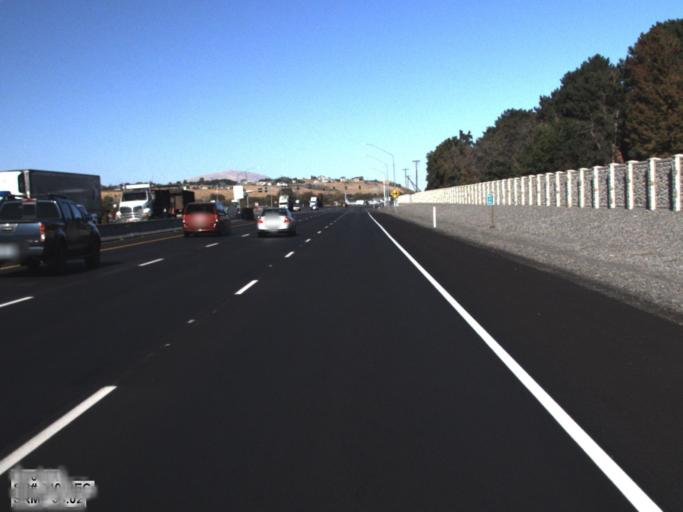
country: US
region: Washington
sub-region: Benton County
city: Richland
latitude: 46.2664
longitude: -119.2996
